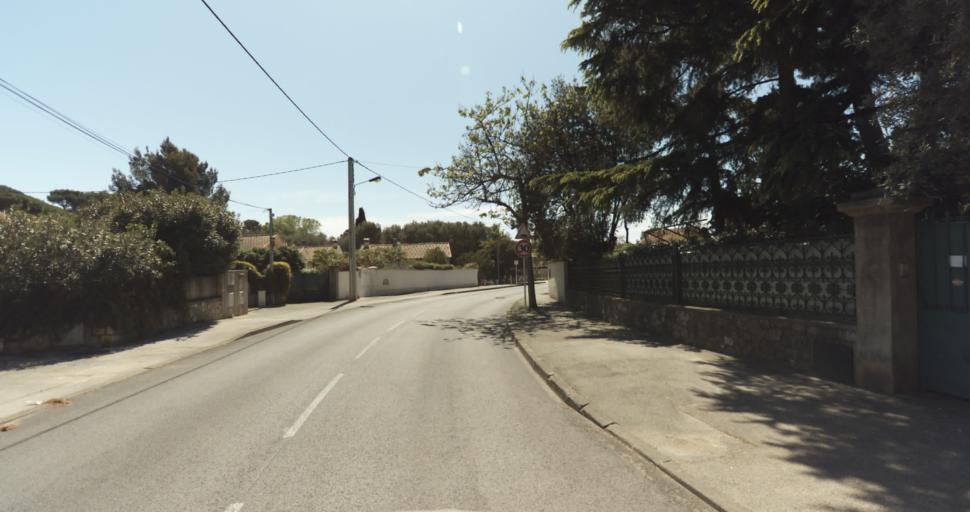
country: FR
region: Provence-Alpes-Cote d'Azur
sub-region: Departement du Var
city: Toulon
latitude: 43.1413
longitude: 5.9028
